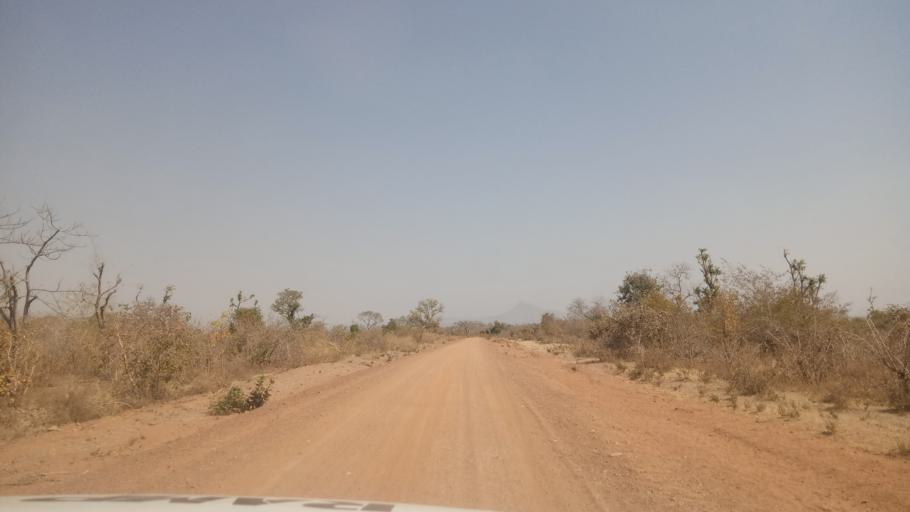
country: NG
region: Adamawa
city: Ngurore
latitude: 9.1628
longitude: 12.1500
